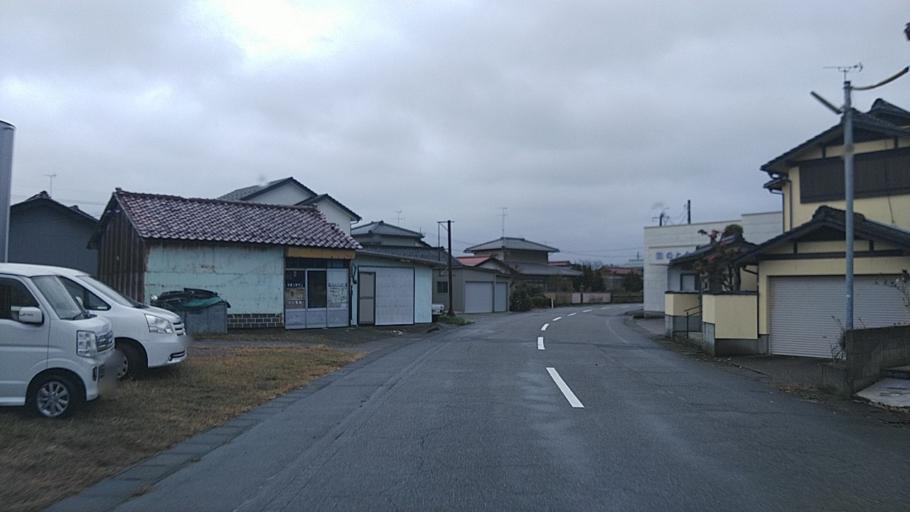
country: JP
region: Ishikawa
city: Komatsu
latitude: 36.3337
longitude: 136.3793
